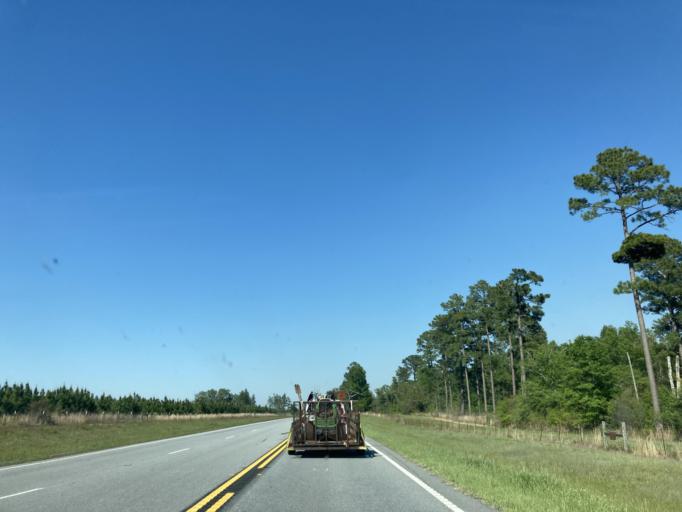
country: US
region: Georgia
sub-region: Dougherty County
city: Putney
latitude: 31.4551
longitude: -84.2567
